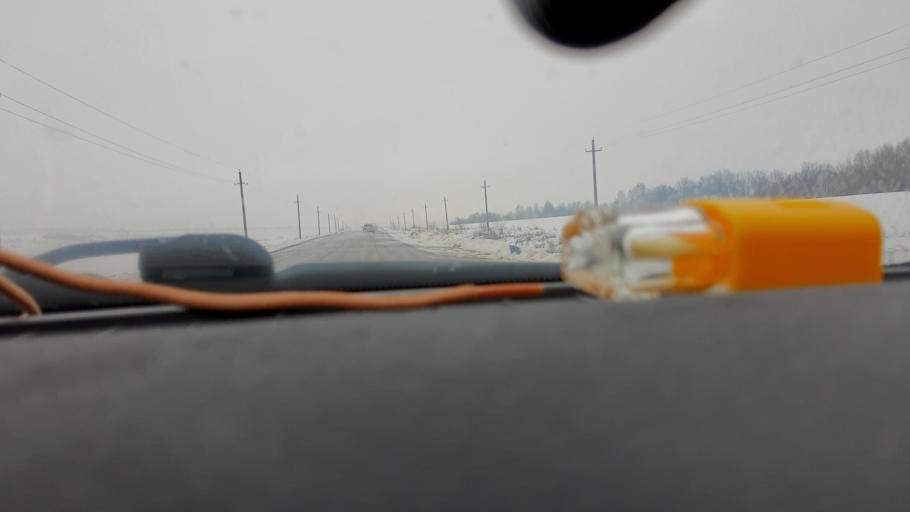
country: RU
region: Bashkortostan
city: Ulukulevo
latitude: 54.5410
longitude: 56.4323
